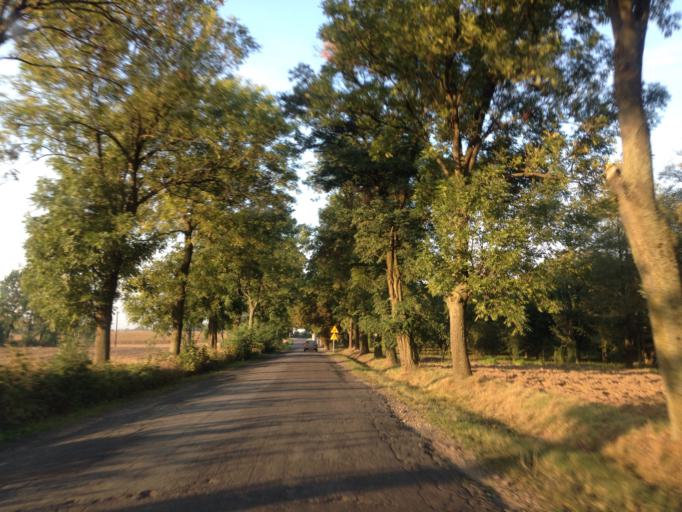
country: PL
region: Kujawsko-Pomorskie
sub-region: Powiat golubsko-dobrzynski
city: Radomin
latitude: 53.1126
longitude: 19.1494
